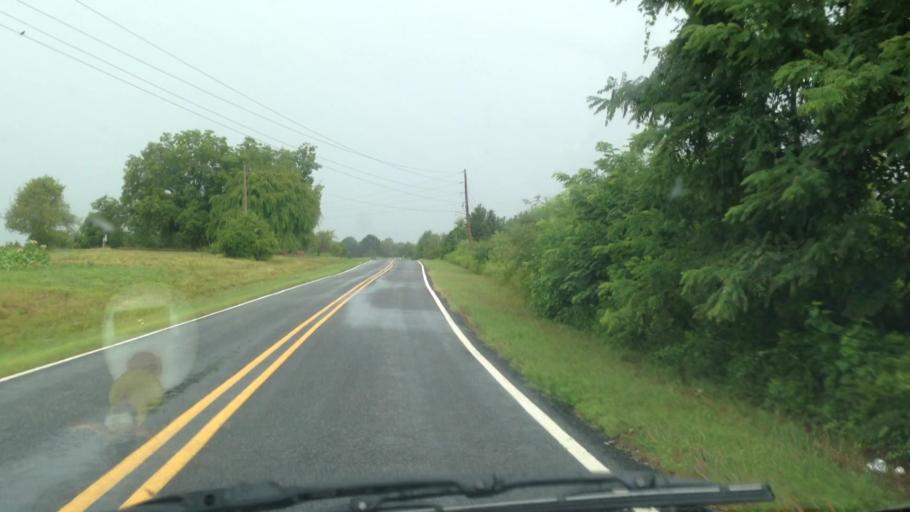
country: US
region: North Carolina
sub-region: Stokes County
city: Danbury
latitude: 36.4439
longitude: -80.0922
